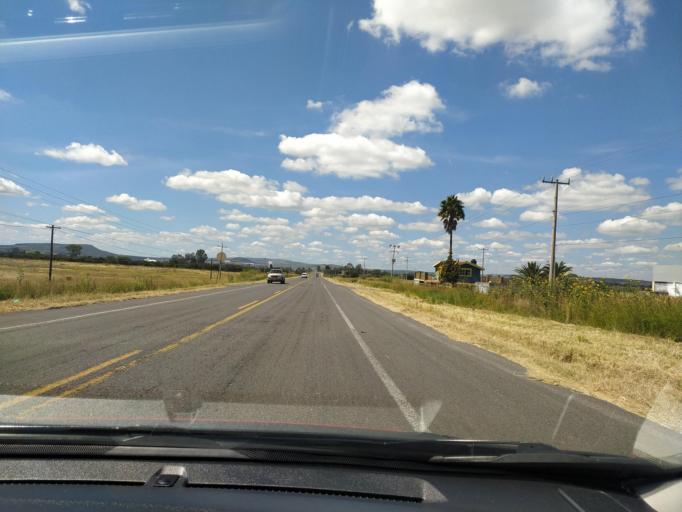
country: MX
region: Jalisco
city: San Miguel el Alto
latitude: 21.0222
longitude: -102.3568
